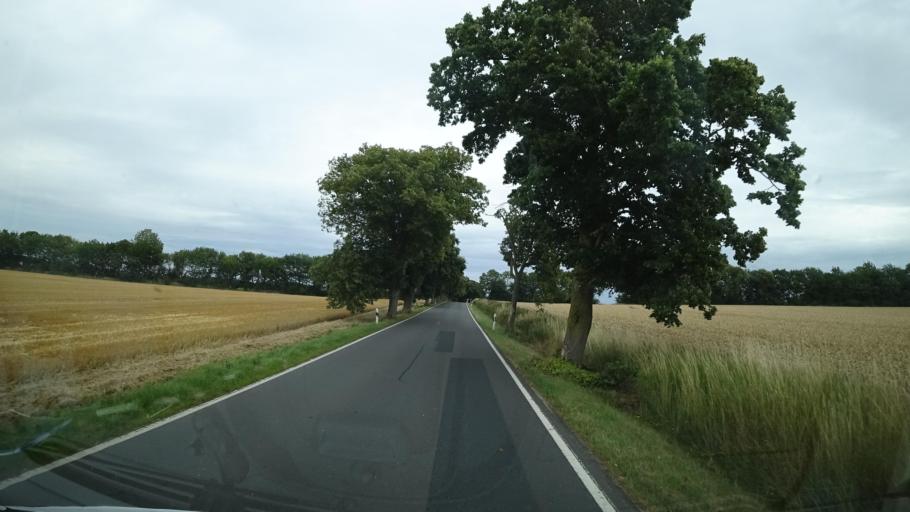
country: DE
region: Mecklenburg-Vorpommern
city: Poseritz
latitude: 54.3032
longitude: 13.2390
